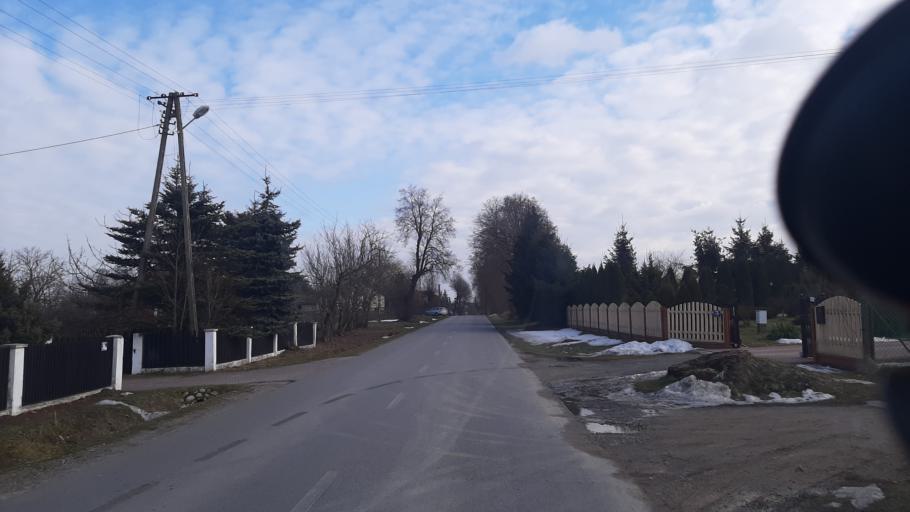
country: PL
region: Lublin Voivodeship
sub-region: Powiat lubartowski
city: Uscimow Stary
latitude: 51.4799
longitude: 22.9133
